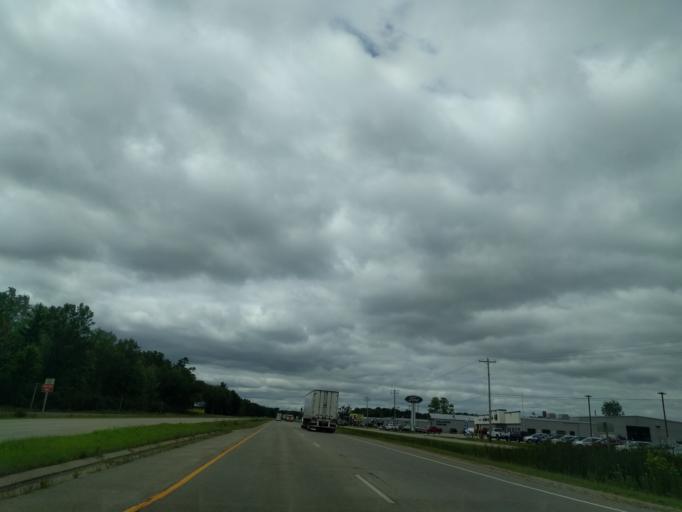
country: US
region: Wisconsin
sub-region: Marinette County
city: Marinette
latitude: 45.0734
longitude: -87.6770
